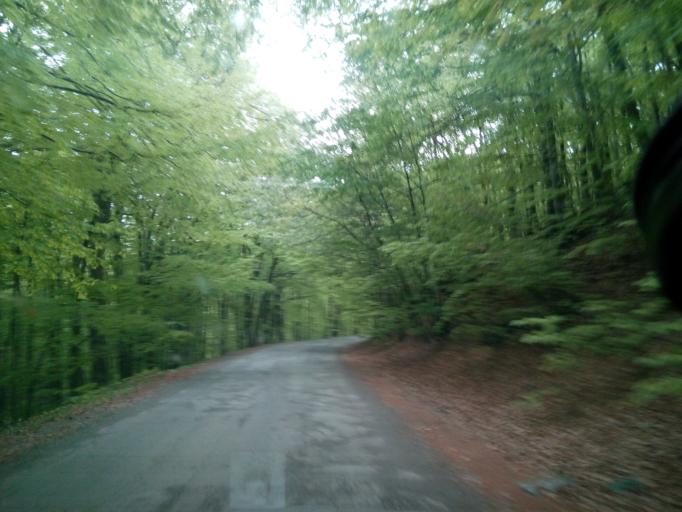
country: SK
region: Kosicky
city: Secovce
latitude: 48.8123
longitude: 21.5199
